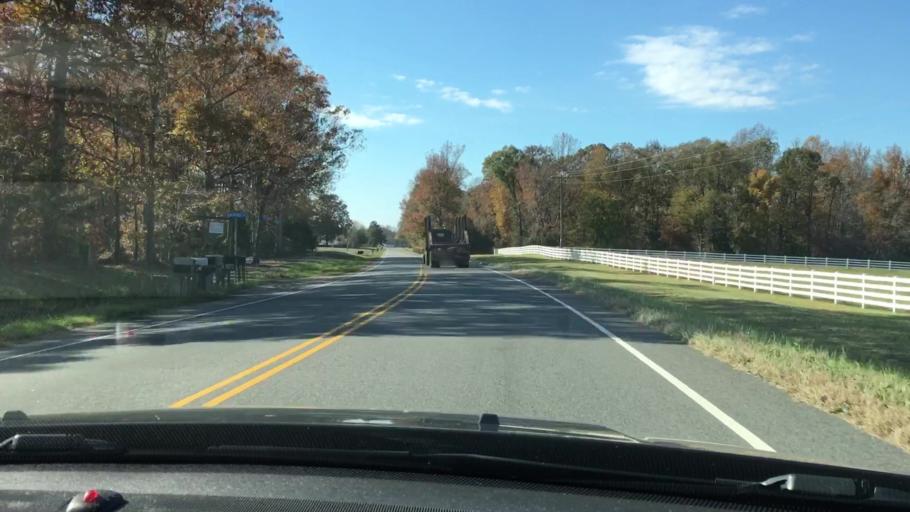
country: US
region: Virginia
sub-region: King William County
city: Central Garage
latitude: 37.7914
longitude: -77.2022
